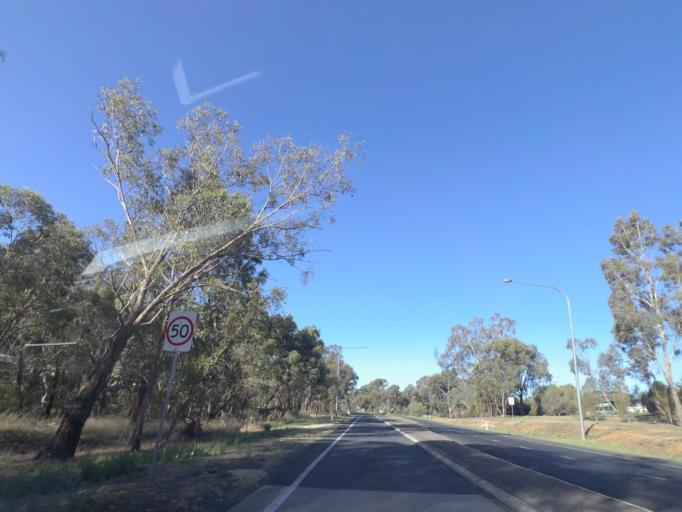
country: AU
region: New South Wales
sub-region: Wagga Wagga
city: Forest Hill
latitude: -35.2746
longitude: 147.7405
